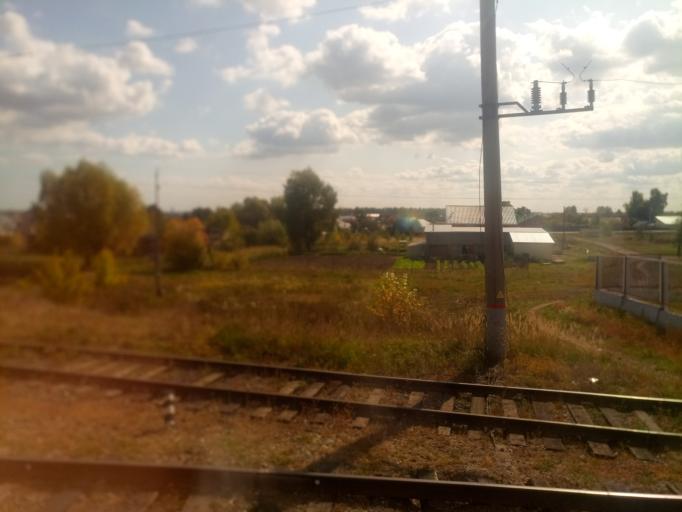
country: RU
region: Chuvashia
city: Urmary
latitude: 55.6896
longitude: 47.9528
